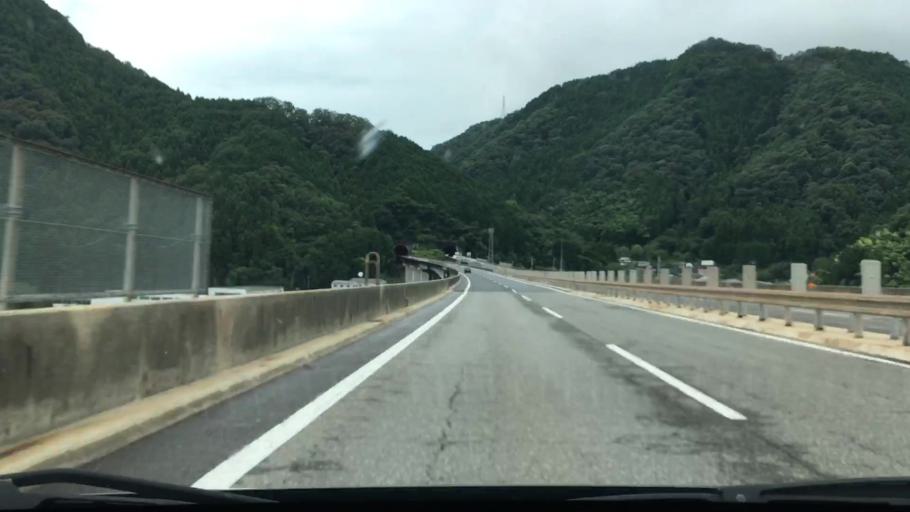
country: JP
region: Hiroshima
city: Hiroshima-shi
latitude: 34.5307
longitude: 132.4362
